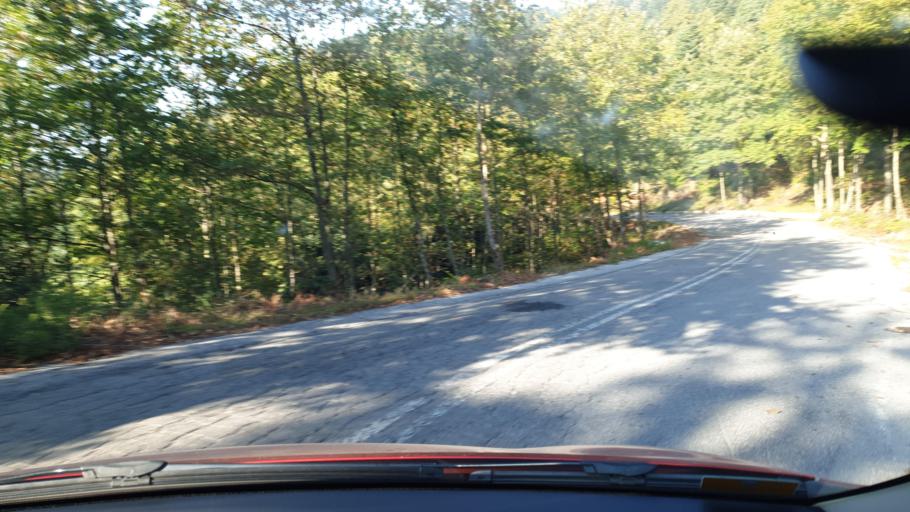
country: GR
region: Central Greece
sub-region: Nomos Evvoias
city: Yimnon
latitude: 38.6036
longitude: 23.9173
